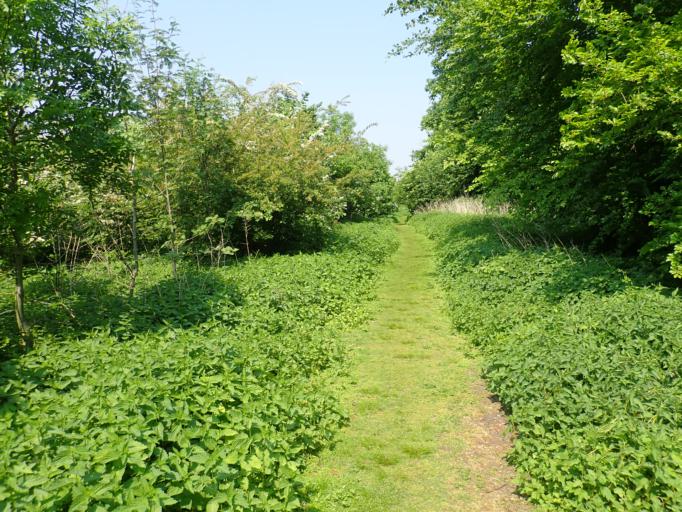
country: BE
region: Flanders
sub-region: Provincie Antwerpen
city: Rumst
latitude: 51.0438
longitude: 4.4338
